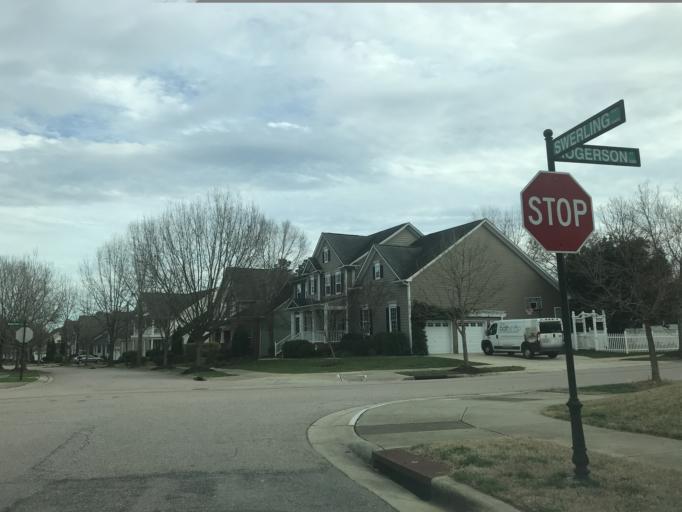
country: US
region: North Carolina
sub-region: Wake County
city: Wake Forest
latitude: 35.9277
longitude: -78.5698
